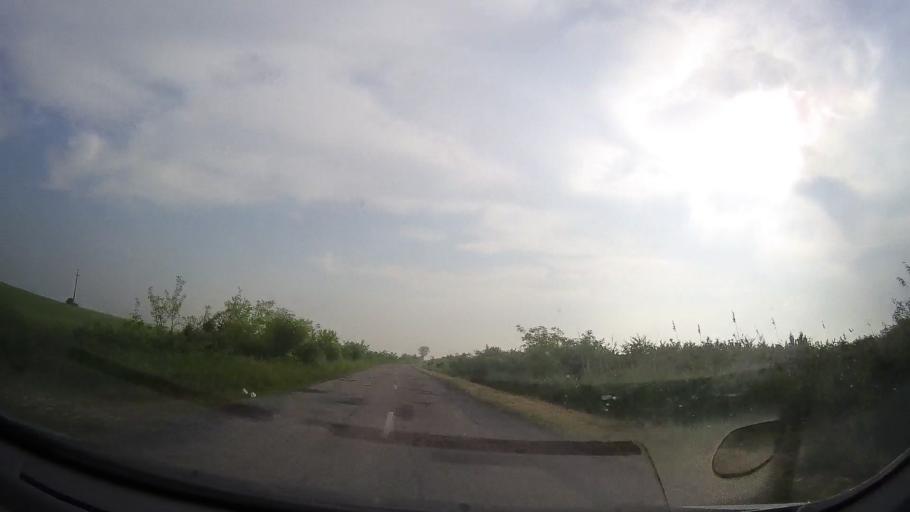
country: RO
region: Timis
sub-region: Comuna Peciu Nou
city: Peciu Nou
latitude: 45.5796
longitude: 21.0221
